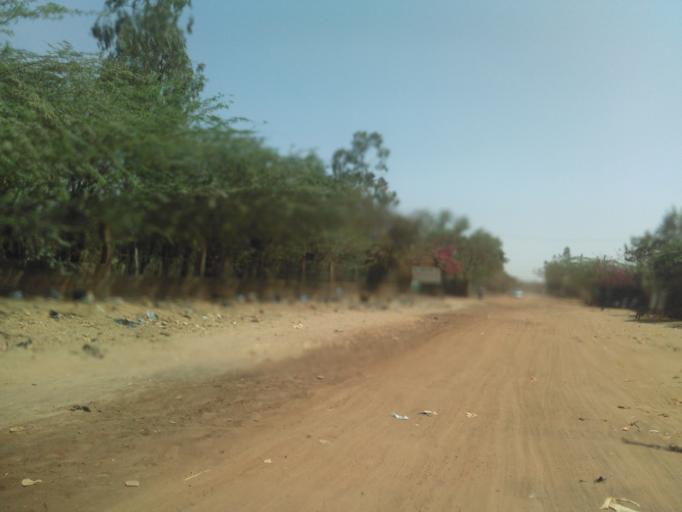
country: BF
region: Centre
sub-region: Kadiogo Province
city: Ouagadougou
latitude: 12.3926
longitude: -1.5707
